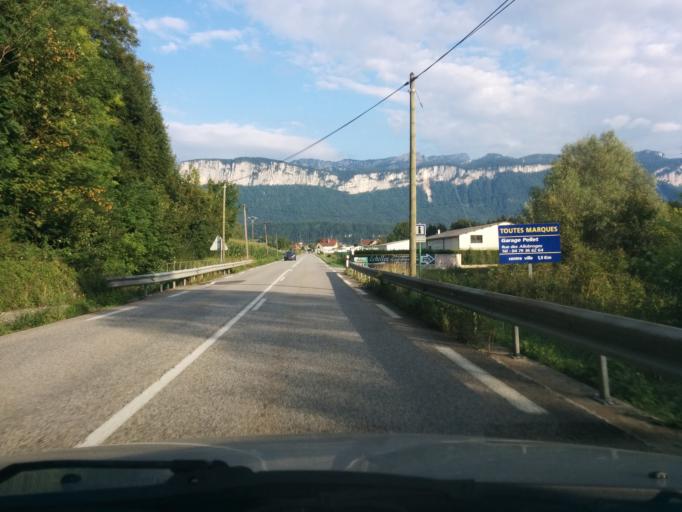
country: FR
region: Rhone-Alpes
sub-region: Departement de la Savoie
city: Les Echelles
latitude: 45.4454
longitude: 5.7400
